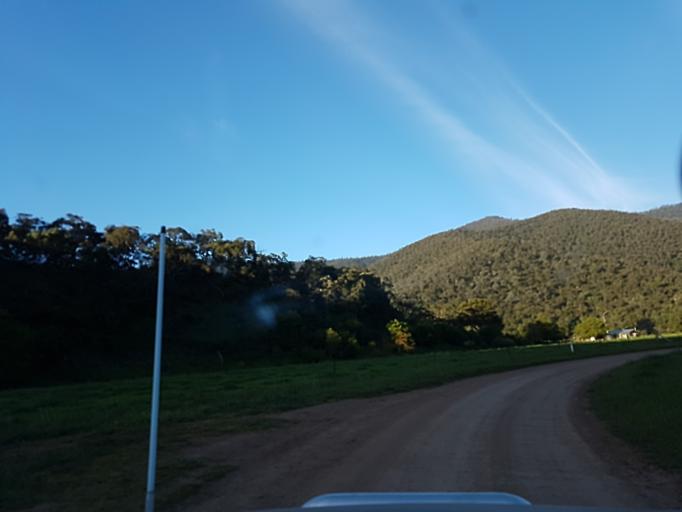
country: AU
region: Victoria
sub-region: East Gippsland
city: Bairnsdale
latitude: -37.4095
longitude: 147.1152
